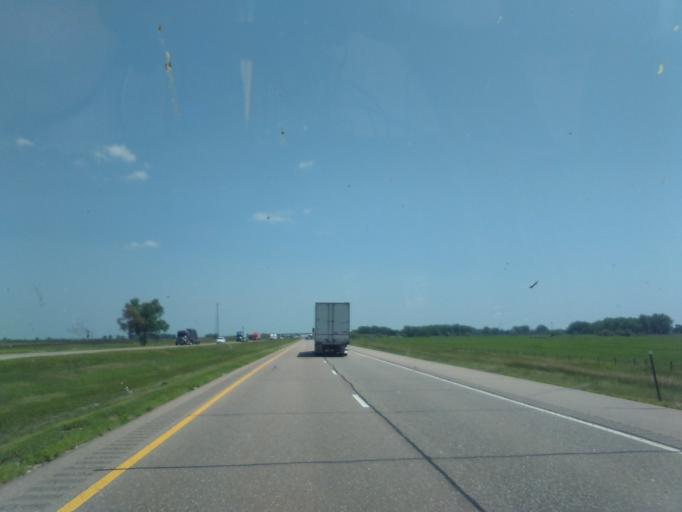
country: US
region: Nebraska
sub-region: Dawson County
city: Gothenburg
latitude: 40.8834
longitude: -100.0822
